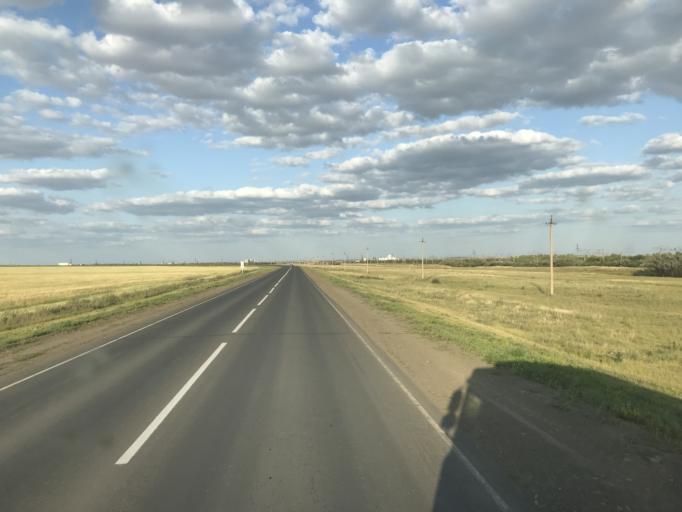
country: KZ
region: Aqmola
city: Atbasar
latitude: 51.7887
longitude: 68.2649
